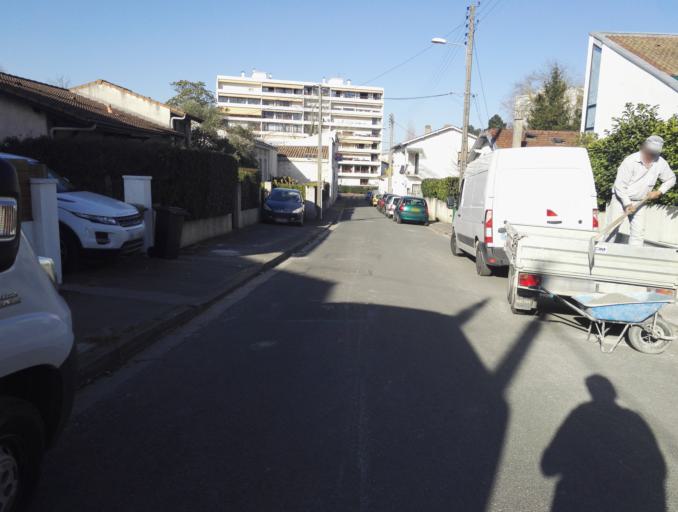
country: FR
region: Aquitaine
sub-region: Departement de la Gironde
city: Talence
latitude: 44.8076
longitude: -0.5831
